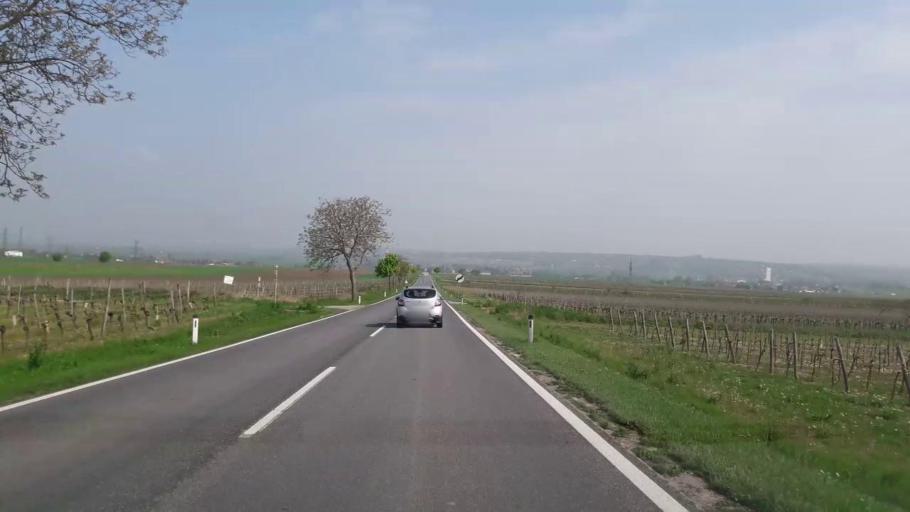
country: AT
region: Lower Austria
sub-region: Politischer Bezirk Hollabrunn
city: Haugsdorf
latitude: 48.6882
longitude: 16.0586
